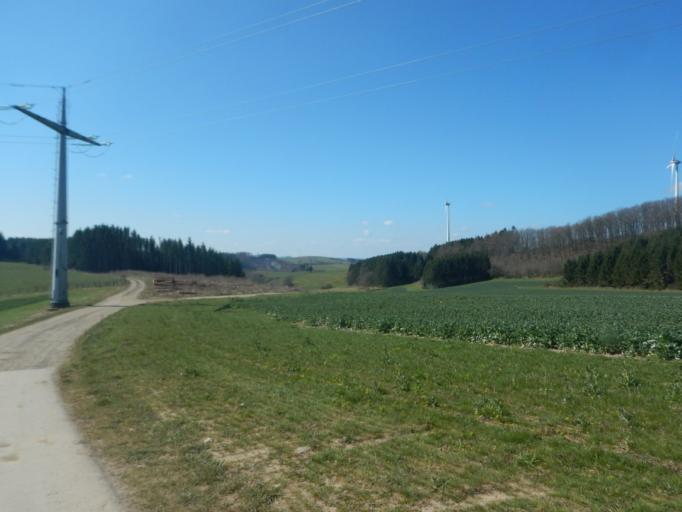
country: LU
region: Diekirch
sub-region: Canton de Clervaux
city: Troisvierges
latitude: 50.1044
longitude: 6.0312
